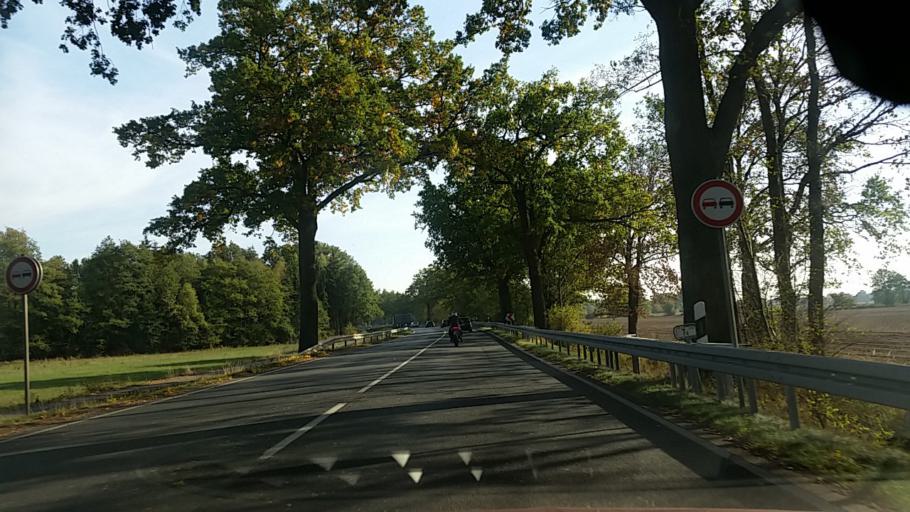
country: DE
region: Lower Saxony
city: Wathlingen
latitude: 52.5654
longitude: 10.1343
